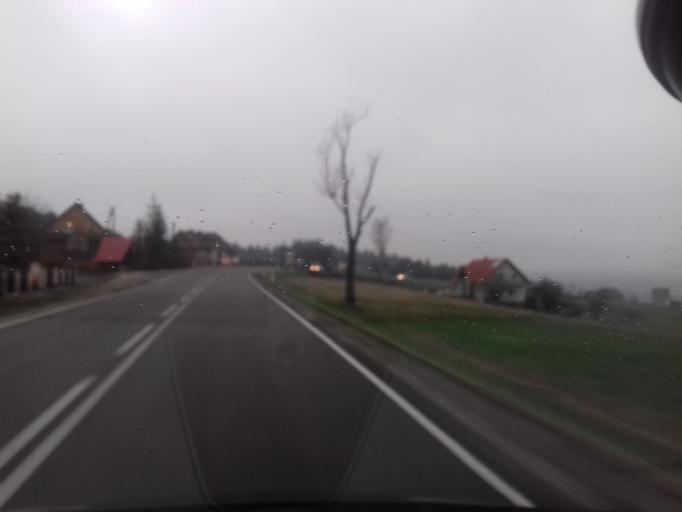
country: PL
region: Lesser Poland Voivodeship
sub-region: Powiat limanowski
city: Kasina Wielka
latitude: 49.6952
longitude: 20.1510
